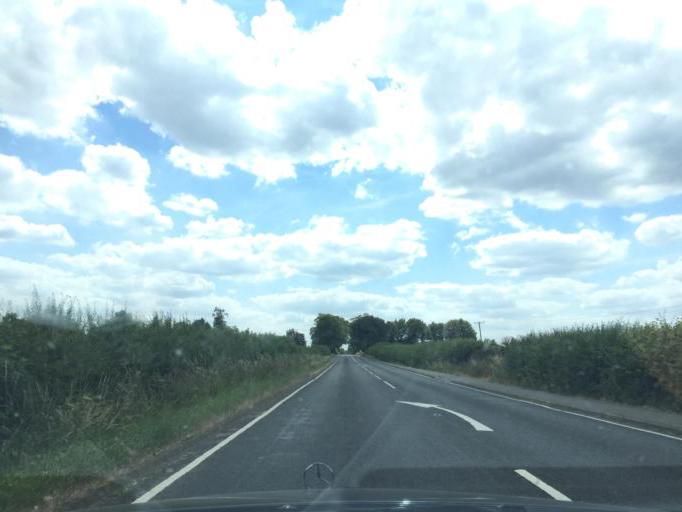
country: GB
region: England
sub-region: Leicestershire
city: Hinckley
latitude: 52.4808
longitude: -1.3719
